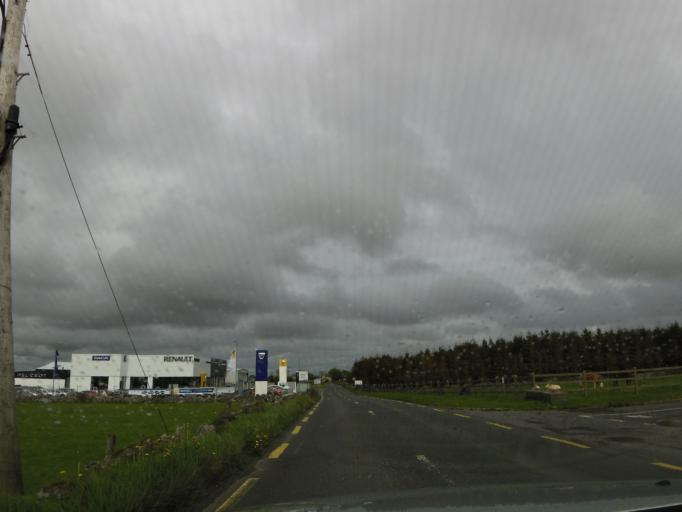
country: IE
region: Connaught
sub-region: Maigh Eo
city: Ballinrobe
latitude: 53.6274
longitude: -9.2141
